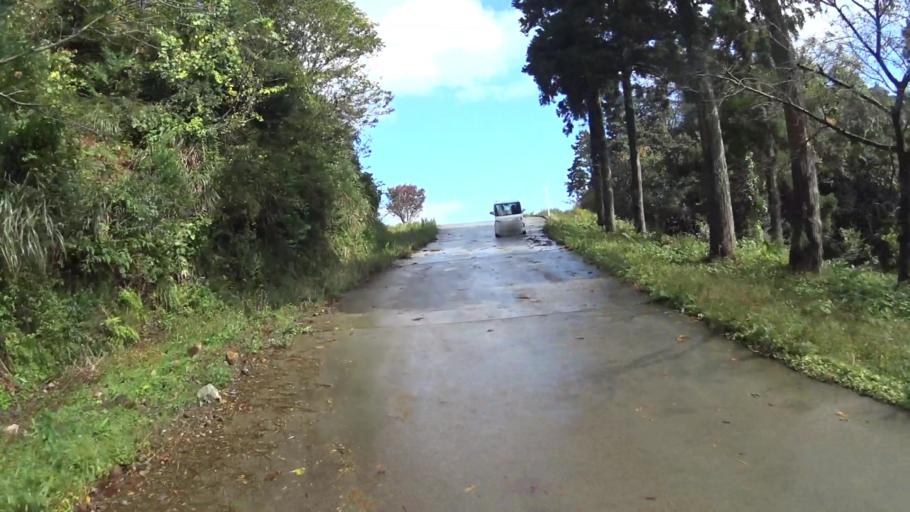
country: JP
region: Kyoto
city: Miyazu
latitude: 35.5991
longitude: 135.1882
